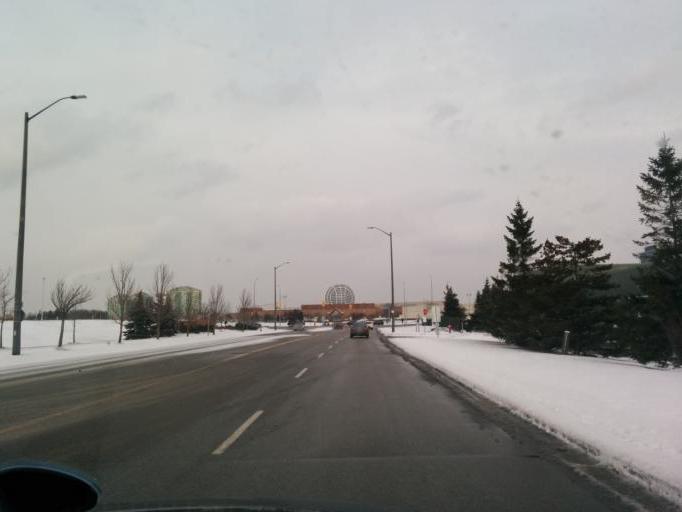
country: CA
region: Ontario
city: Mississauga
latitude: 43.5547
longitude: -79.7160
